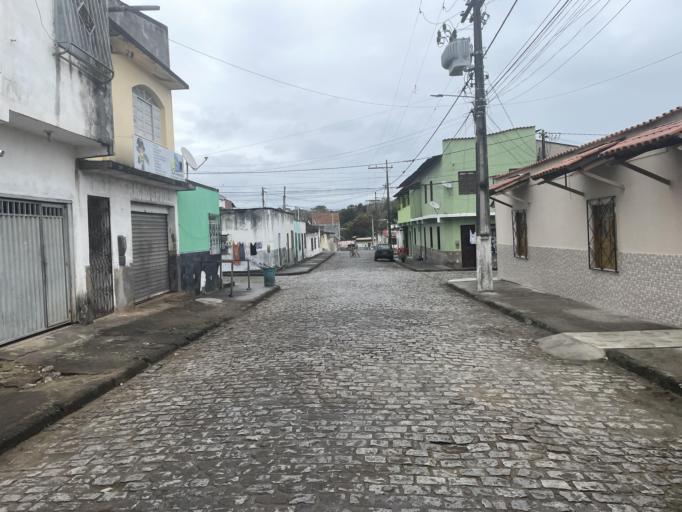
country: BR
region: Bahia
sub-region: Urucuca
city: Urucuca
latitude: -14.5894
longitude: -39.2858
